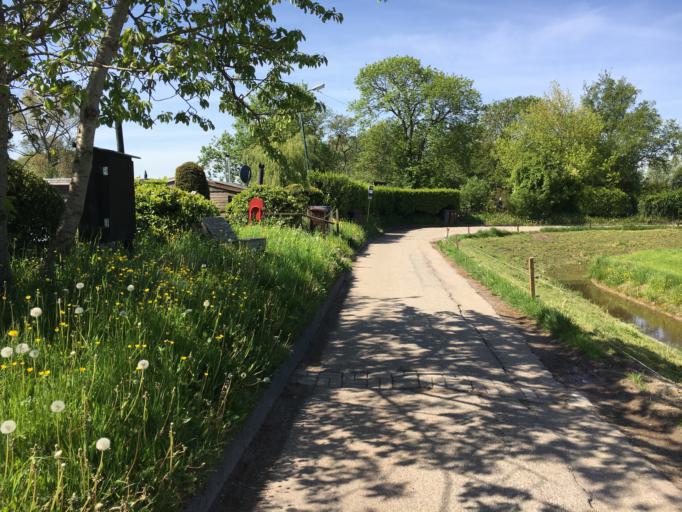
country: NL
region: North Holland
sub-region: Gemeente Weesp
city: Weesp
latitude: 52.2851
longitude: 5.0589
